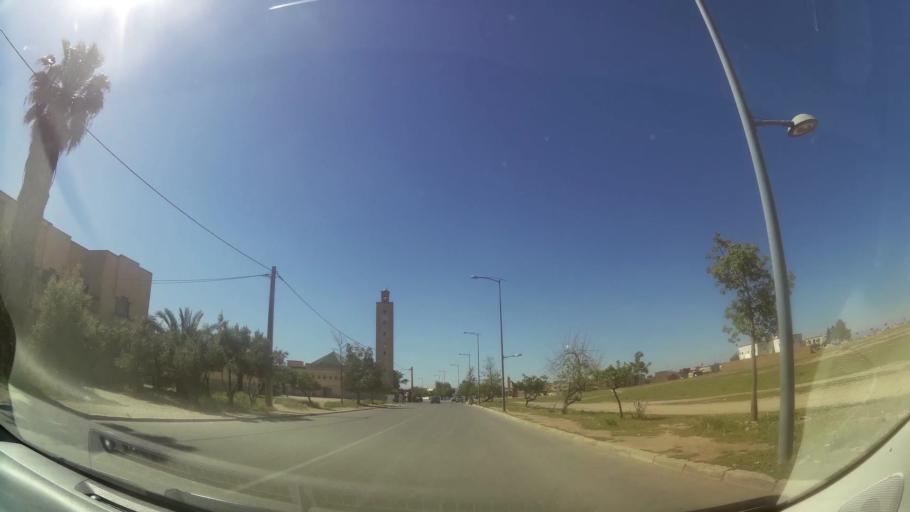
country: MA
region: Oriental
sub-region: Oujda-Angad
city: Oujda
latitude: 34.6644
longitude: -1.8681
